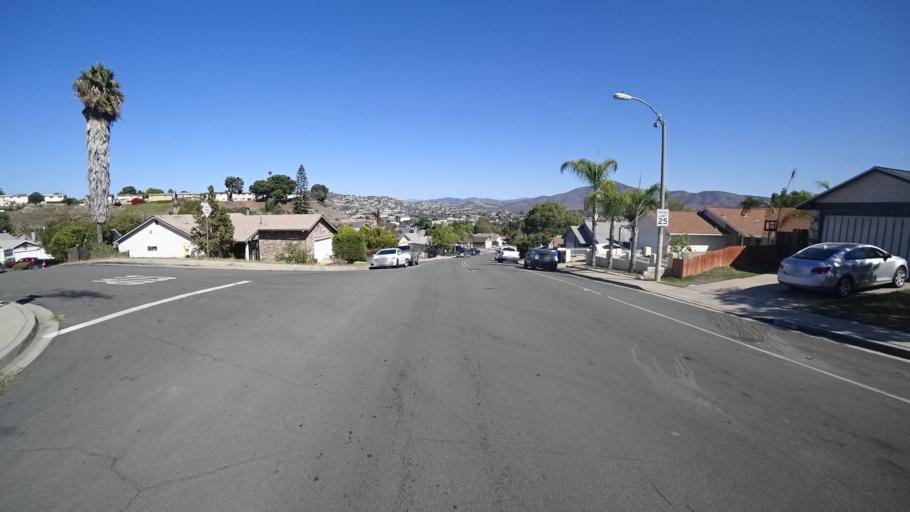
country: US
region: California
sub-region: San Diego County
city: La Presa
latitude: 32.7038
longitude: -117.0241
